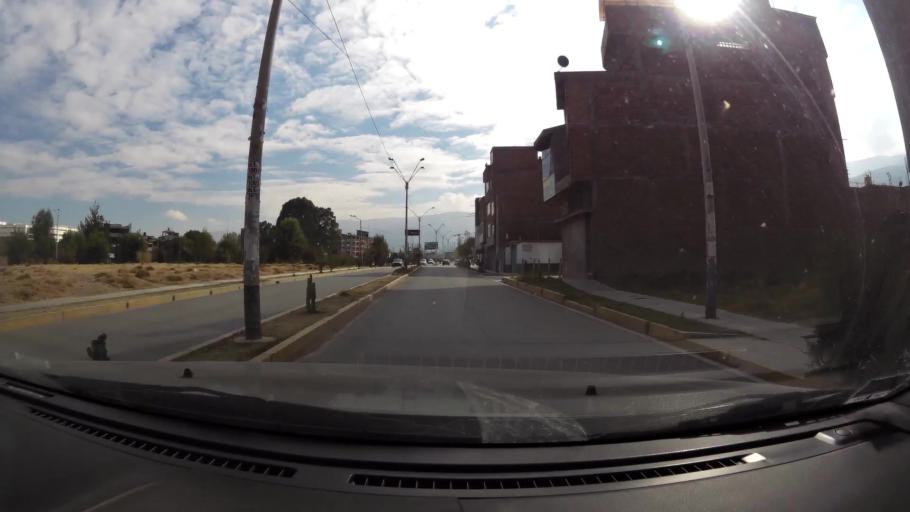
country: PE
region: Junin
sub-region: Provincia de Huancayo
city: Huancayo
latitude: -12.0513
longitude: -75.1964
